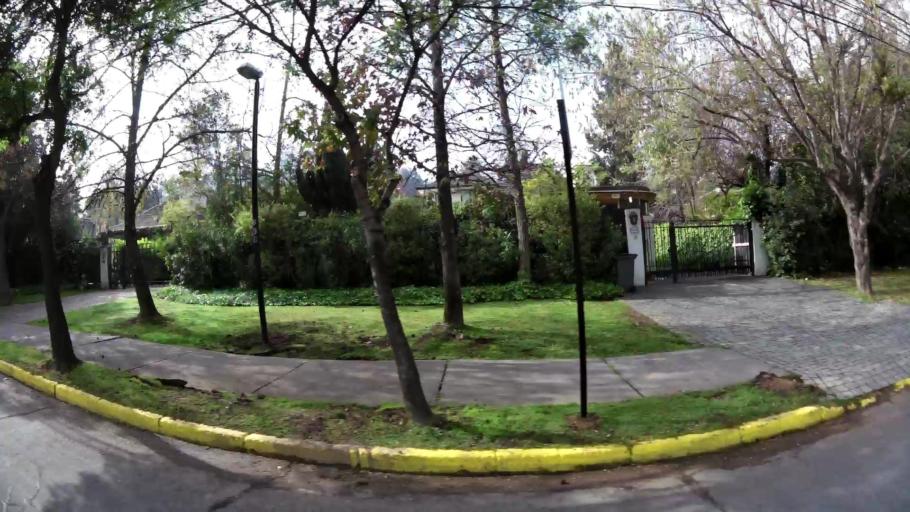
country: CL
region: Santiago Metropolitan
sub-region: Provincia de Santiago
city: Villa Presidente Frei, Nunoa, Santiago, Chile
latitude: -33.3762
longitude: -70.5292
